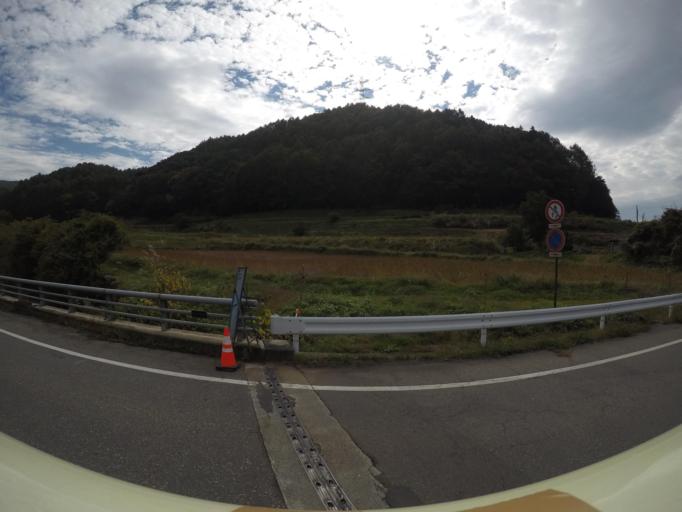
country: JP
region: Nagano
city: Ina
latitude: 35.8559
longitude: 138.0790
